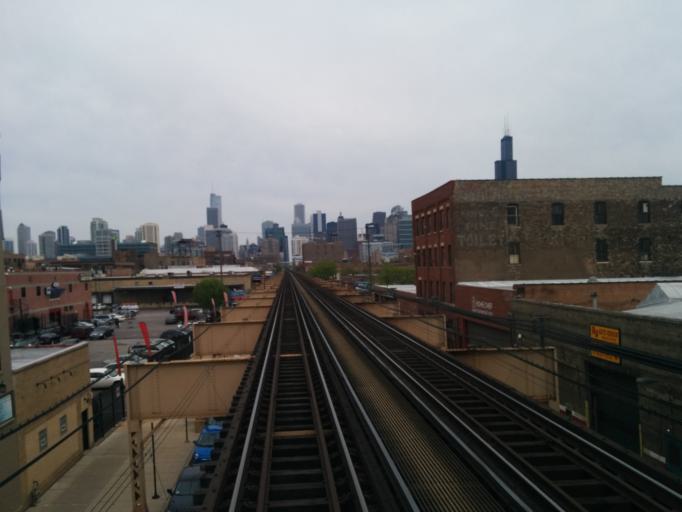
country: US
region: Illinois
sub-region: Cook County
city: Chicago
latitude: 41.8855
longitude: -87.6602
